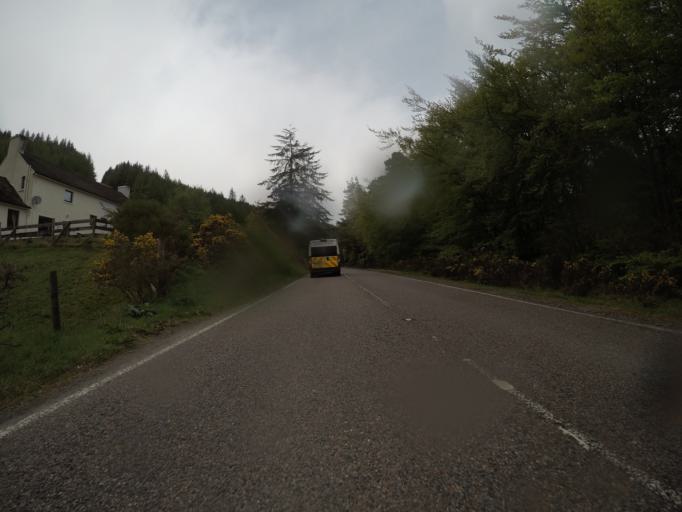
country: GB
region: Scotland
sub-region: Highland
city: Spean Bridge
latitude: 57.0457
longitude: -4.8043
